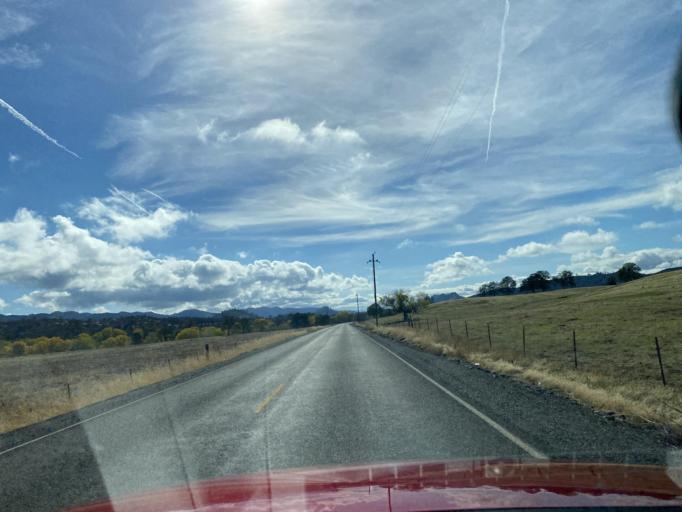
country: US
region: California
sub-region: Glenn County
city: Willows
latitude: 39.4670
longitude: -122.5120
